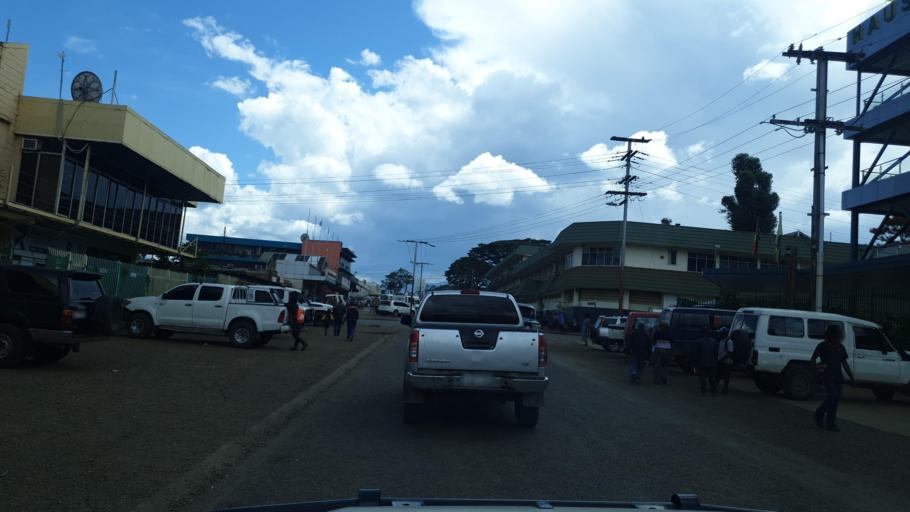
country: PG
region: Eastern Highlands
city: Goroka
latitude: -6.0729
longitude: 145.3960
